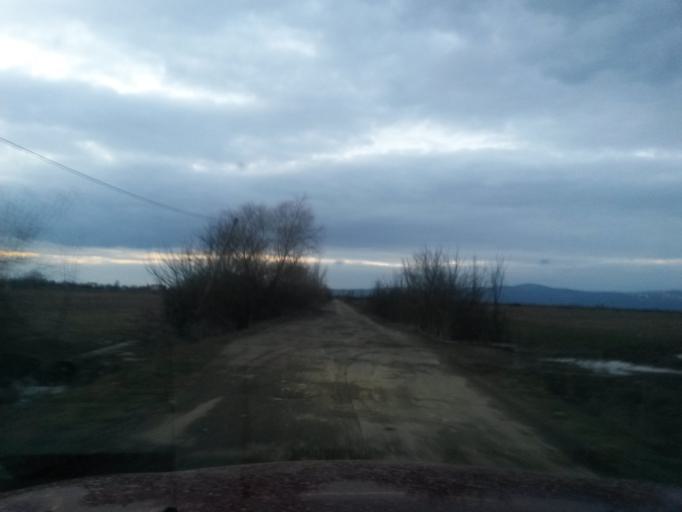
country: SK
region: Kosicky
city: Sobrance
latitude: 48.6898
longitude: 22.0518
